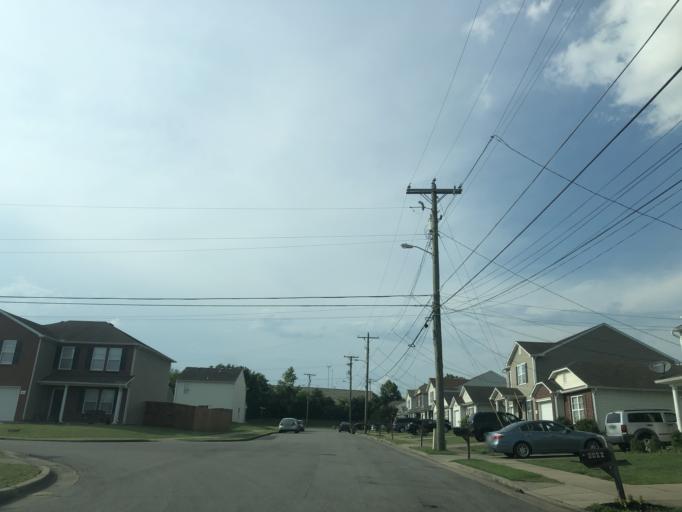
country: US
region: Tennessee
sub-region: Davidson County
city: Nashville
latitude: 36.2351
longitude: -86.7935
